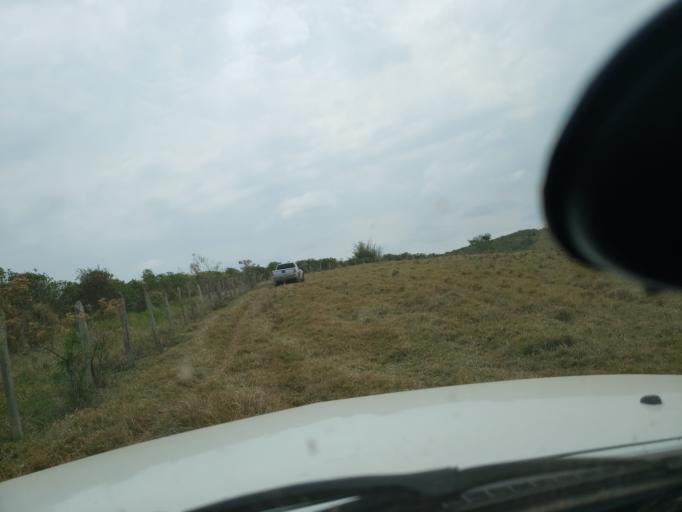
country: BR
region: Minas Gerais
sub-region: Jacutinga
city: Jacutinga
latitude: -22.3434
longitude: -46.5871
